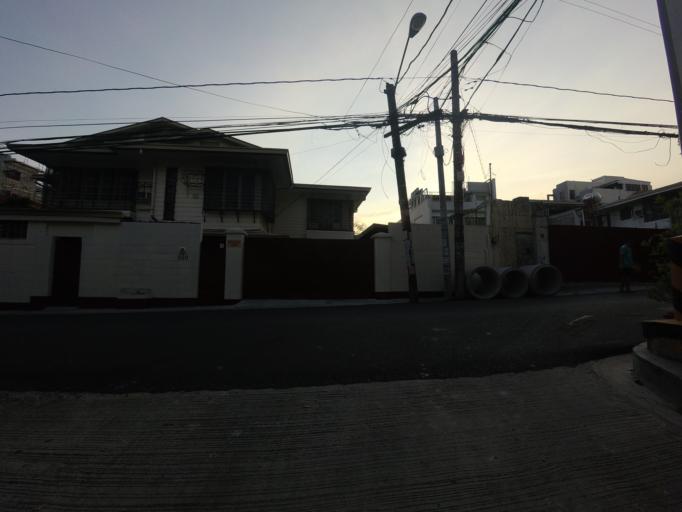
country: PH
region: Metro Manila
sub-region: San Juan
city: San Juan
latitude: 14.5997
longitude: 121.0311
